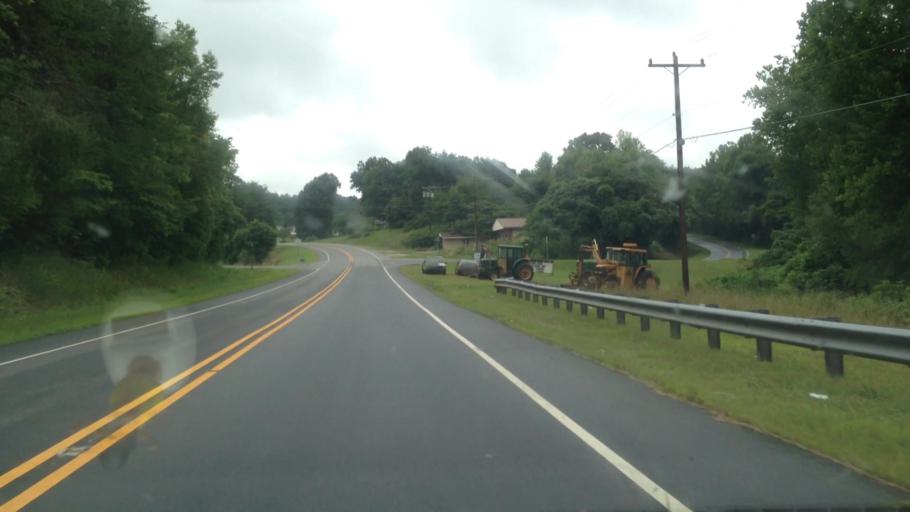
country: US
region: North Carolina
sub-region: Rockingham County
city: Mayodan
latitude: 36.4090
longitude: -79.9892
